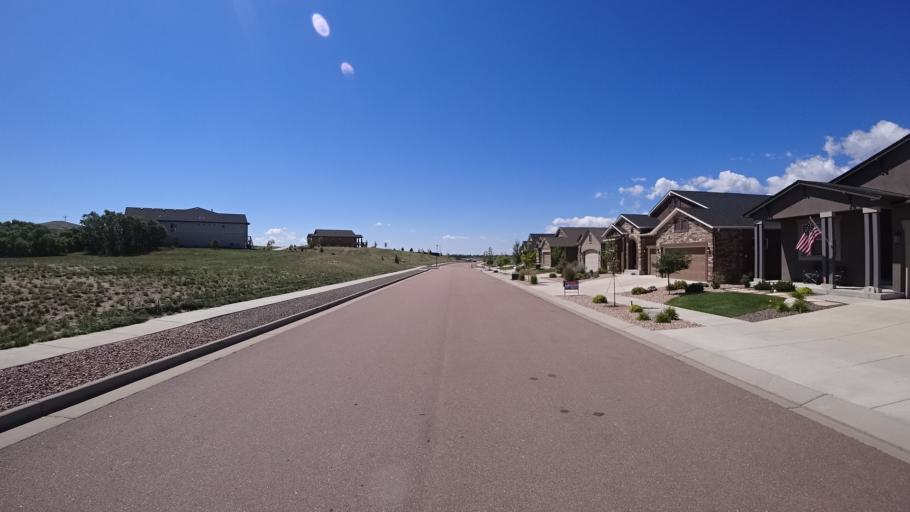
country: US
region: Colorado
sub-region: El Paso County
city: Black Forest
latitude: 38.9861
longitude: -104.7588
